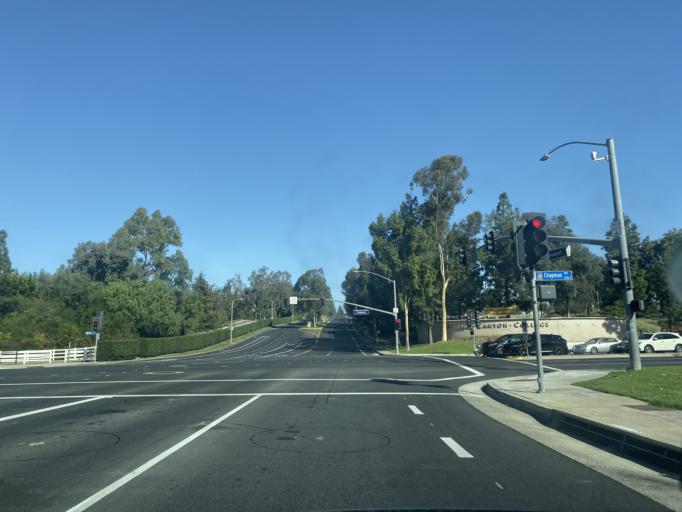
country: US
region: California
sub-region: Orange County
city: North Tustin
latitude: 33.7948
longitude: -117.7717
